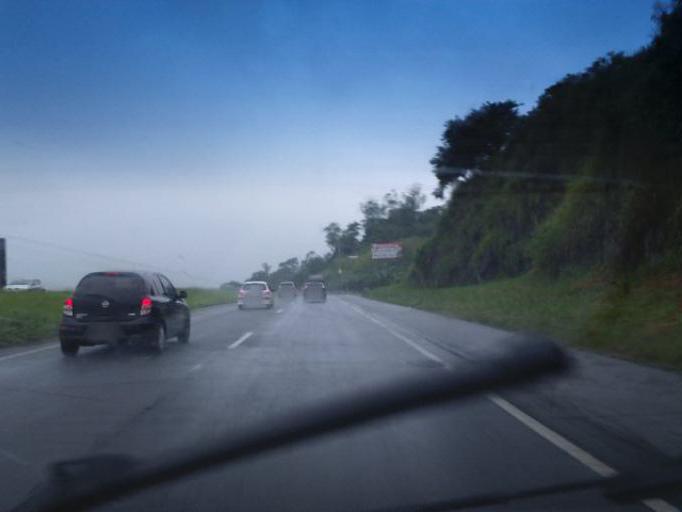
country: BR
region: Sao Paulo
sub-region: Miracatu
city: Miracatu
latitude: -24.2852
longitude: -47.4401
